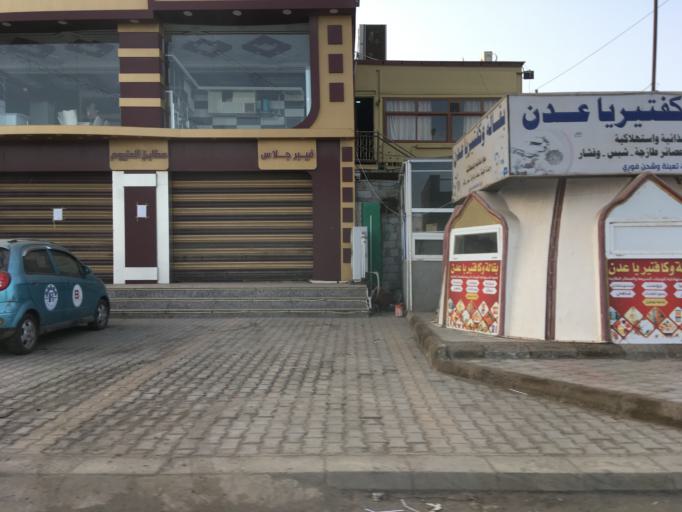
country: YE
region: Aden
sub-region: Ash Shaikh Outhman
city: Ash Shaykh `Uthman
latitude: 12.8597
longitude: 45.0097
